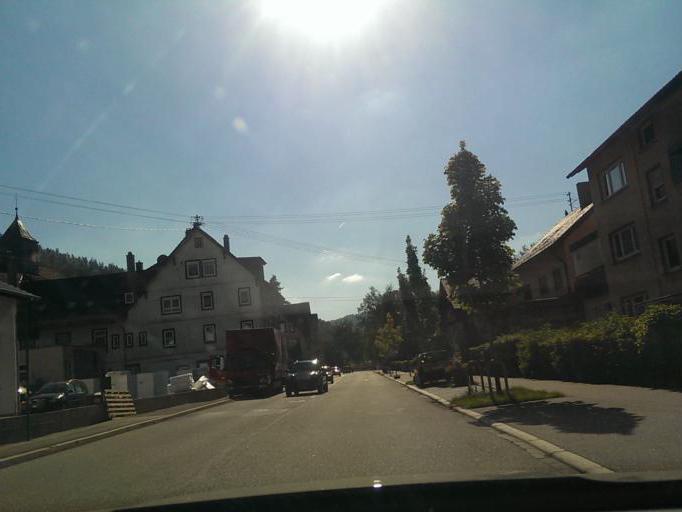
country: DE
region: Baden-Wuerttemberg
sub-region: Karlsruhe Region
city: Hofen an der Enz
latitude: 48.8036
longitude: 8.5834
